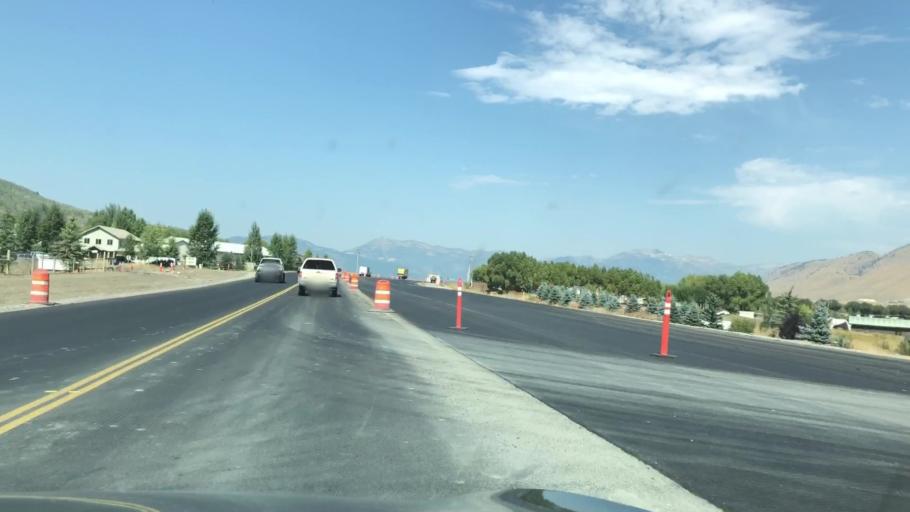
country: US
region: Wyoming
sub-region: Teton County
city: South Park
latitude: 43.3711
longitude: -110.7407
